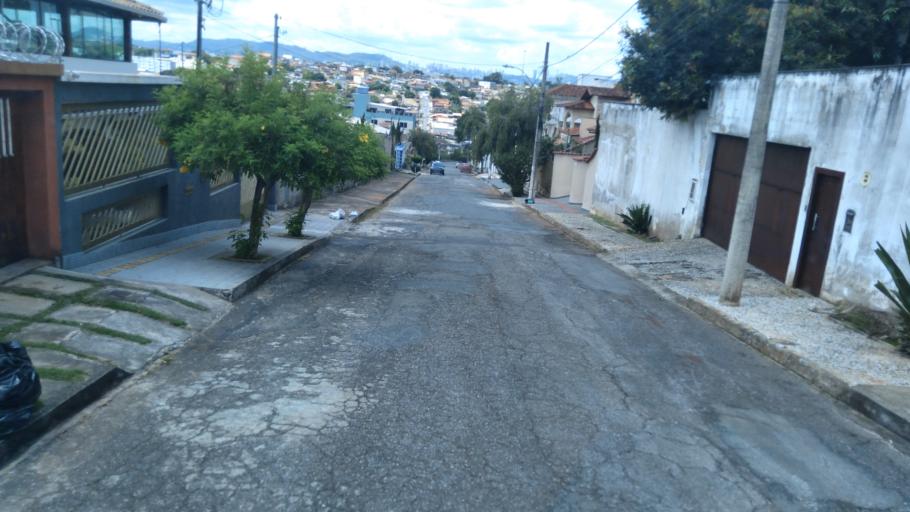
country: BR
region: Minas Gerais
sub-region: Contagem
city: Contagem
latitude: -19.9156
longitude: -44.0081
